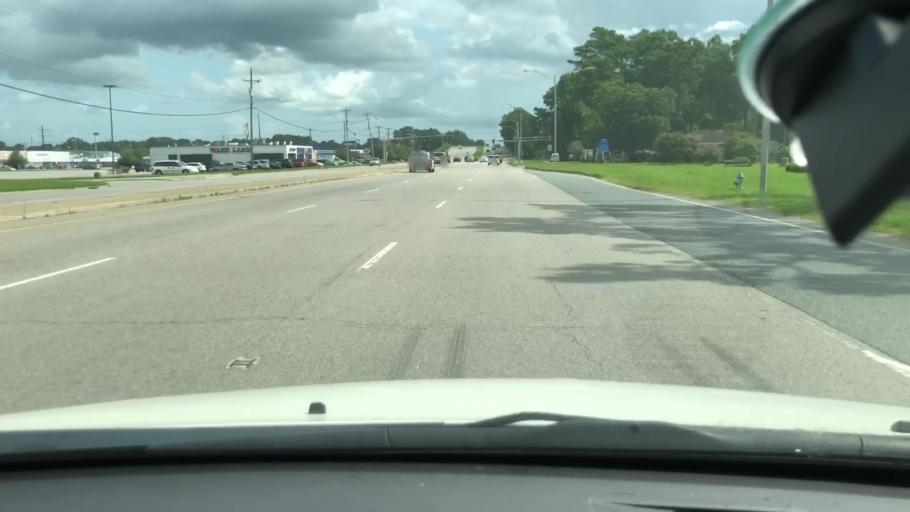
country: US
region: Virginia
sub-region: City of Chesapeake
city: Chesapeake
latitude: 36.7839
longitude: -76.2570
